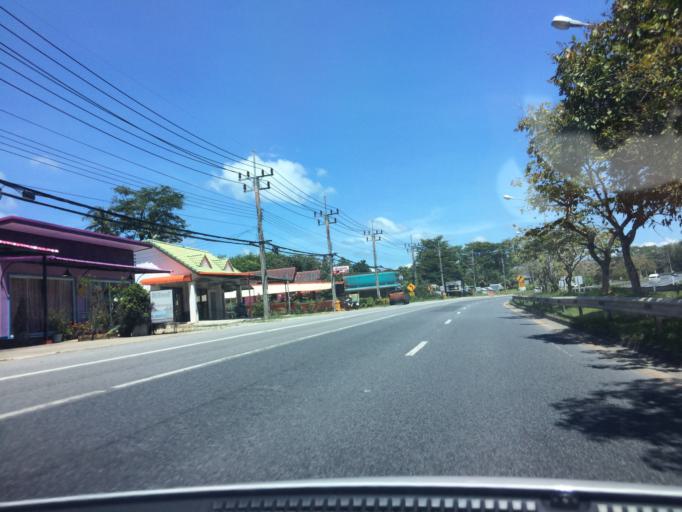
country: TH
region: Phuket
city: Thalang
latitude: 8.1280
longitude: 98.3375
